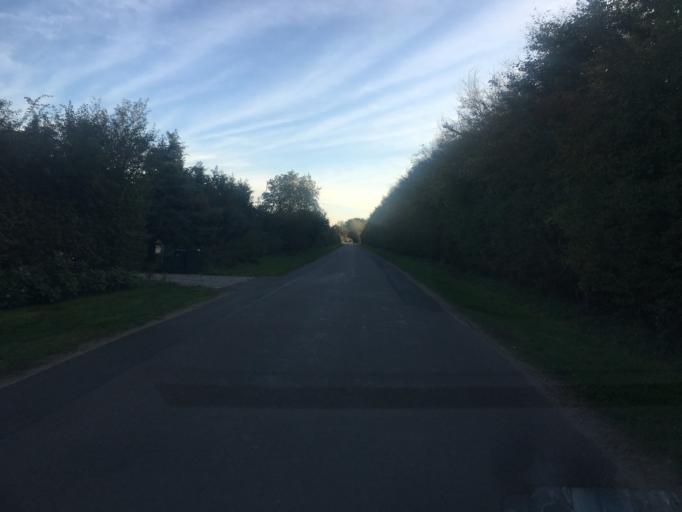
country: DE
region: Schleswig-Holstein
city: Ellhoft
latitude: 54.9136
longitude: 8.9918
